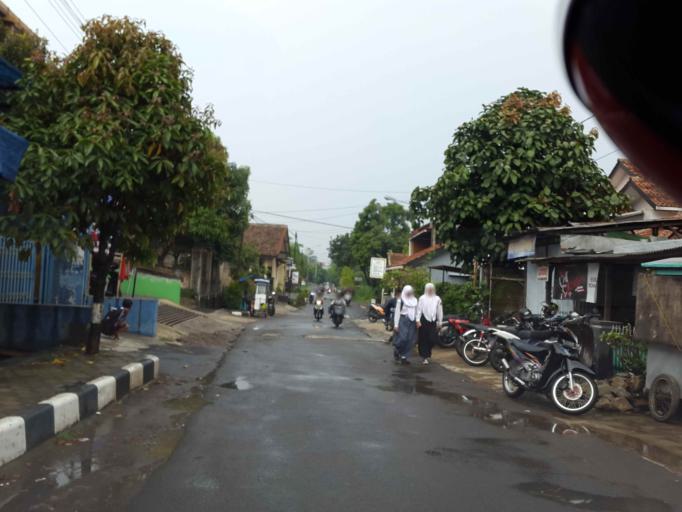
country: ID
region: West Java
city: Cimahi
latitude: -6.8585
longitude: 107.5544
